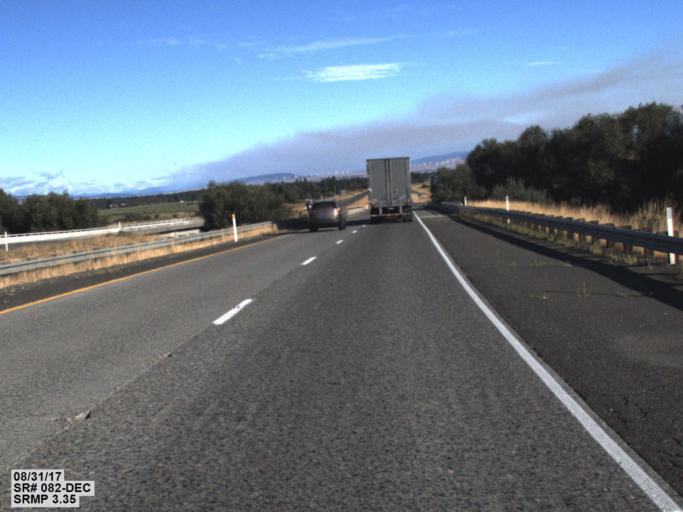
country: US
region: Washington
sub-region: Kittitas County
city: Ellensburg
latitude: 46.9249
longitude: -120.4968
